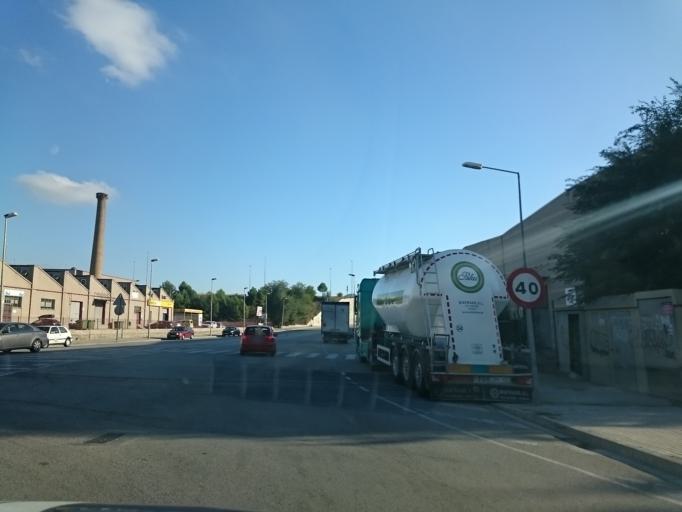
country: ES
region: Catalonia
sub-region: Provincia de Barcelona
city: Palleja
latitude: 41.4170
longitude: 2.0003
